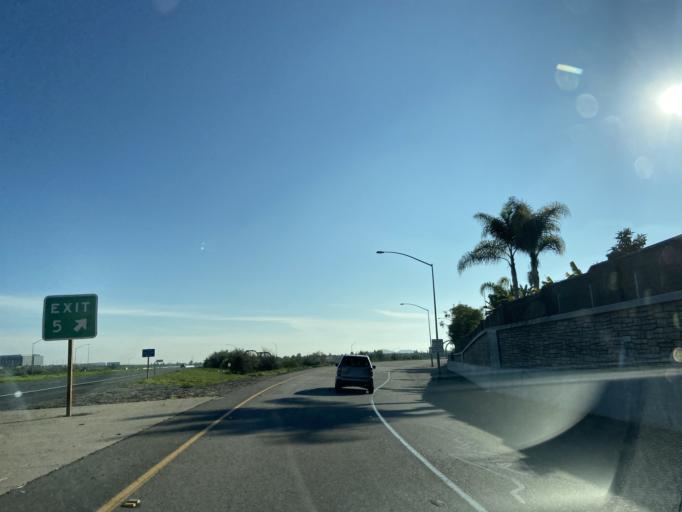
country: US
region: California
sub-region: San Diego County
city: Bonita
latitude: 32.6240
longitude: -116.9717
